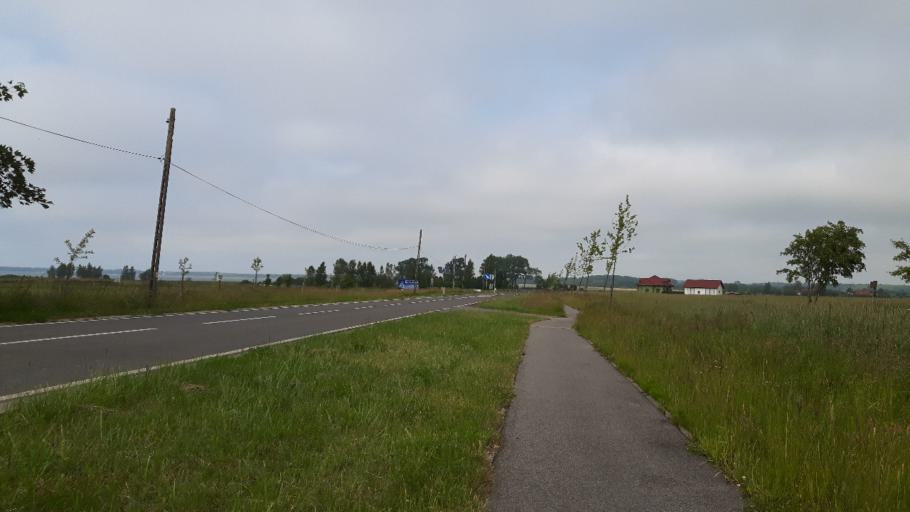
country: PL
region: West Pomeranian Voivodeship
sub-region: Powiat koszalinski
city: Sianow
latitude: 54.3372
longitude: 16.3173
